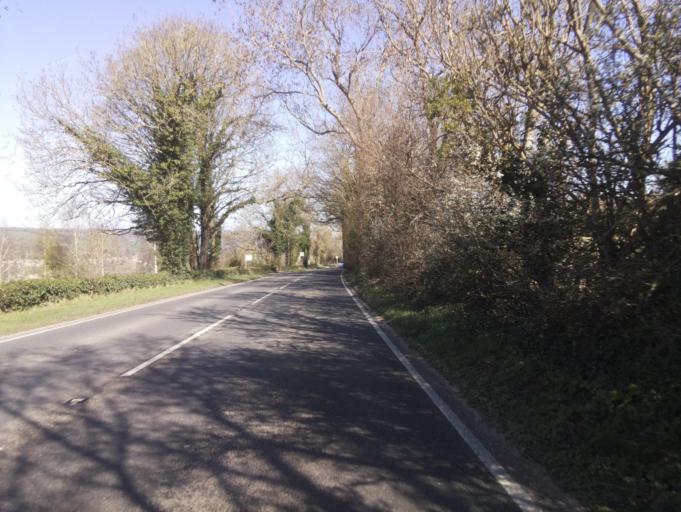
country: GB
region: England
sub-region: Bath and North East Somerset
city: Freshford
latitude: 51.3917
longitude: -2.3041
